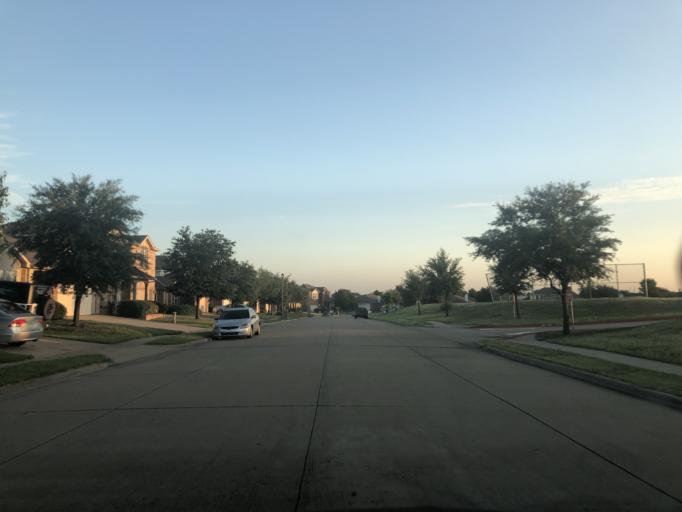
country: US
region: Texas
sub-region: Dallas County
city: Cedar Hill
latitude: 32.6530
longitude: -96.9759
